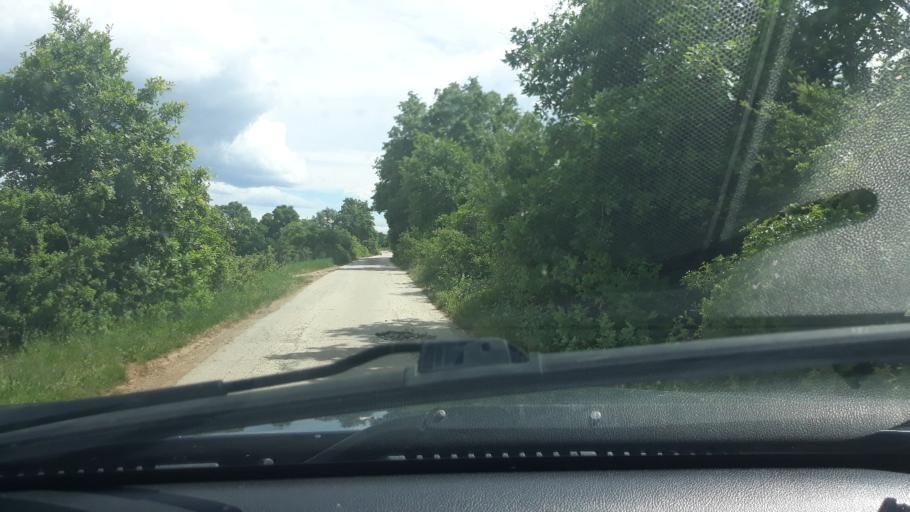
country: MK
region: Krivogastani
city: Krivogashtani
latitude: 41.3287
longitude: 21.3030
